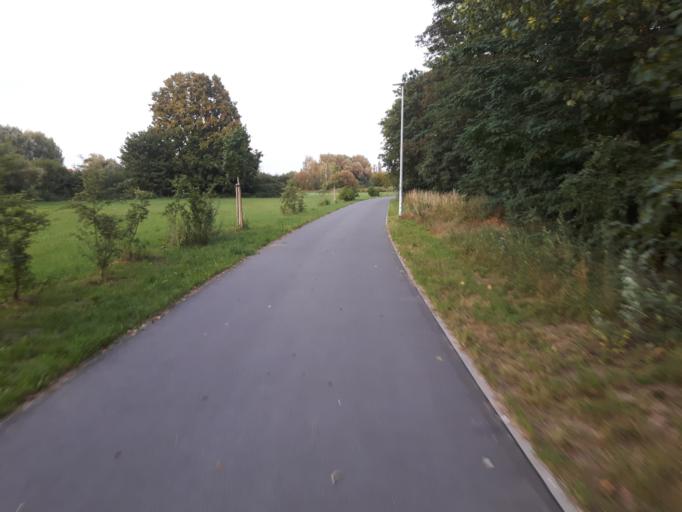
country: DE
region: Berlin
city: Staaken
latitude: 52.5571
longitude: 13.1261
